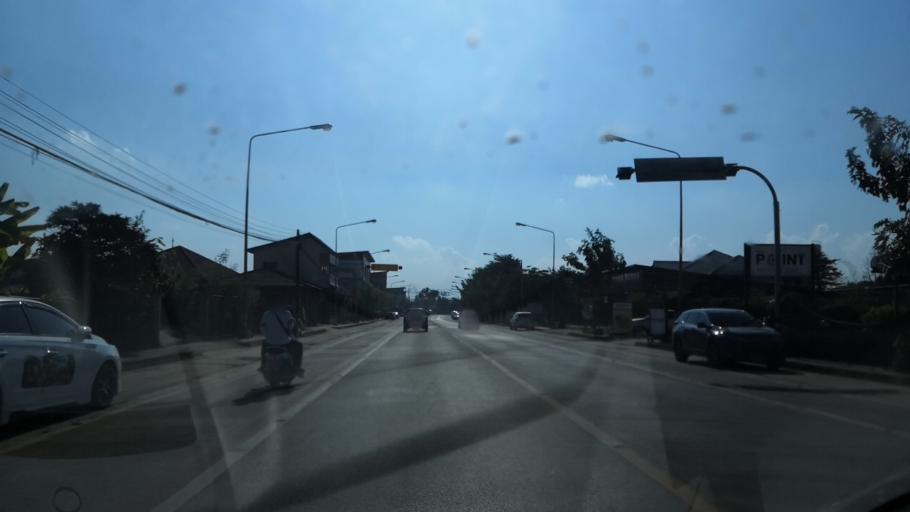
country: TH
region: Chiang Rai
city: Chiang Rai
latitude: 19.9359
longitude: 99.8430
